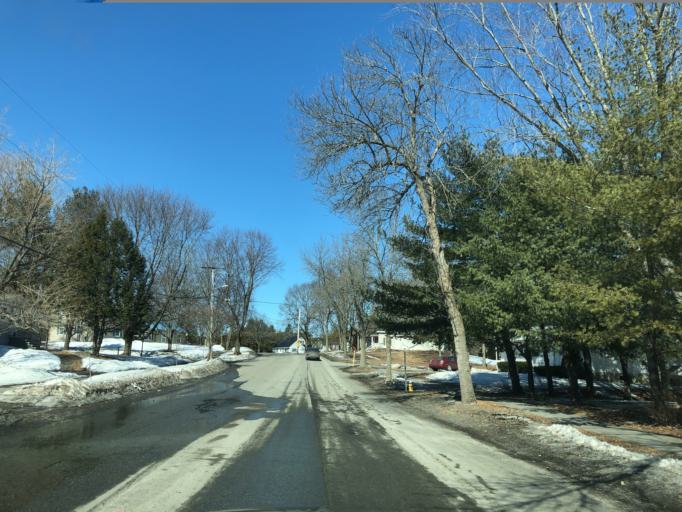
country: US
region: Maine
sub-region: Penobscot County
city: Brewer
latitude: 44.8164
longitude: -68.7539
